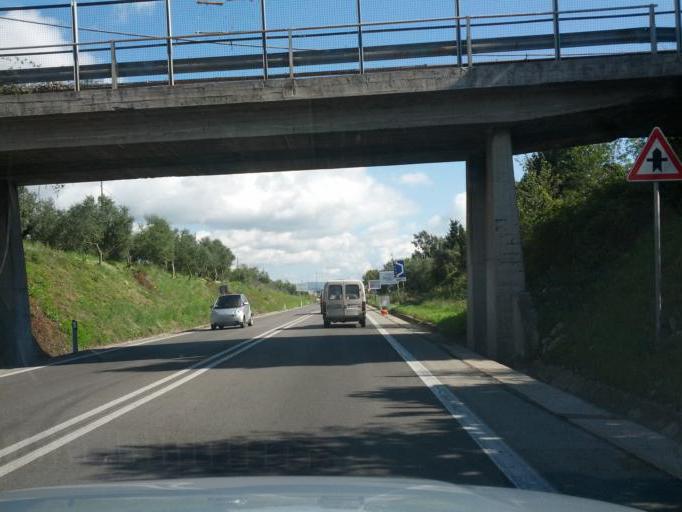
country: IT
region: Latium
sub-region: Provincia di Latina
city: Formia
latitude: 41.2667
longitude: 13.6601
